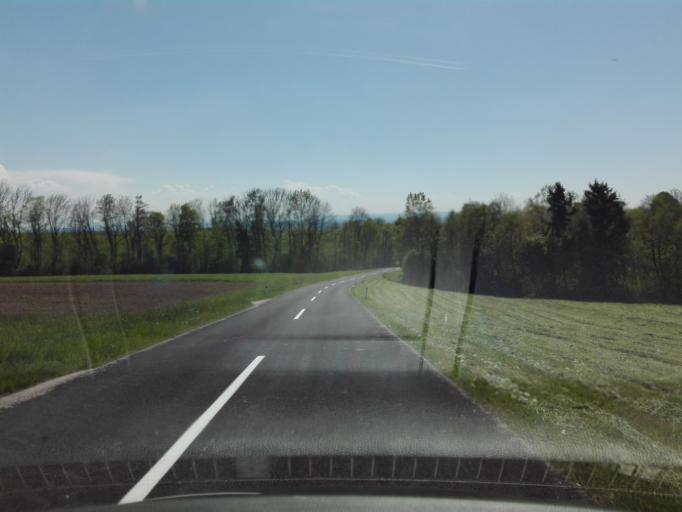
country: AT
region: Upper Austria
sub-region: Politischer Bezirk Rohrbach
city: Kleinzell im Muehlkreis
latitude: 48.3614
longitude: 13.9179
